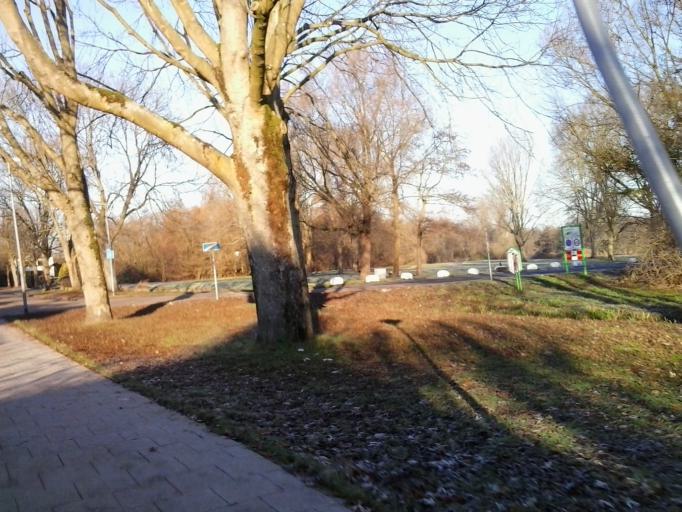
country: NL
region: South Holland
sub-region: Gemeente Lansingerland
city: Bergschenhoek
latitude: 51.9646
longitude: 4.5075
